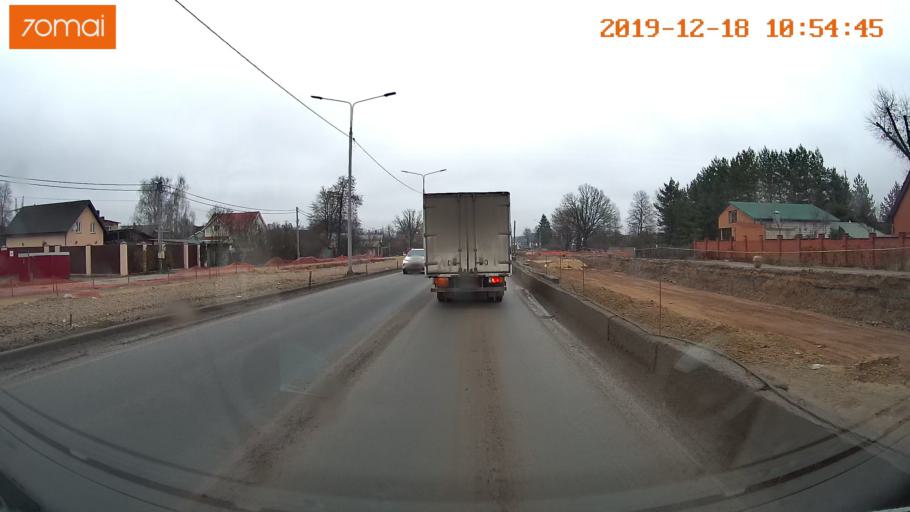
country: RU
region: Moskovskaya
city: Selyatino
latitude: 55.5340
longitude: 36.9822
